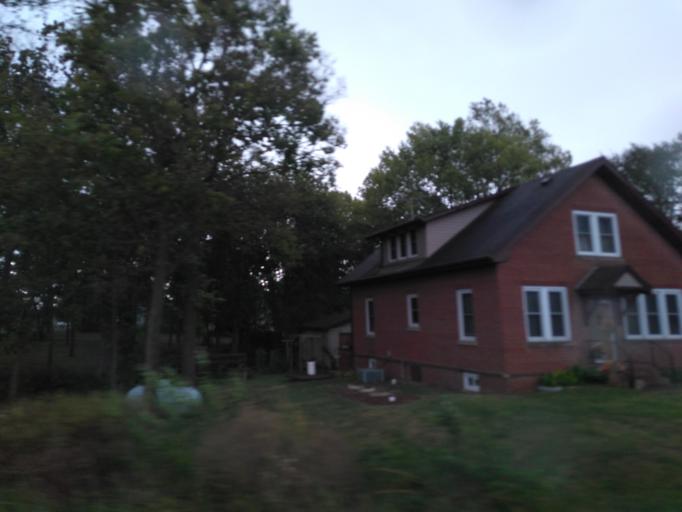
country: US
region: Illinois
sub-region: Madison County
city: Highland
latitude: 38.7587
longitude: -89.6600
